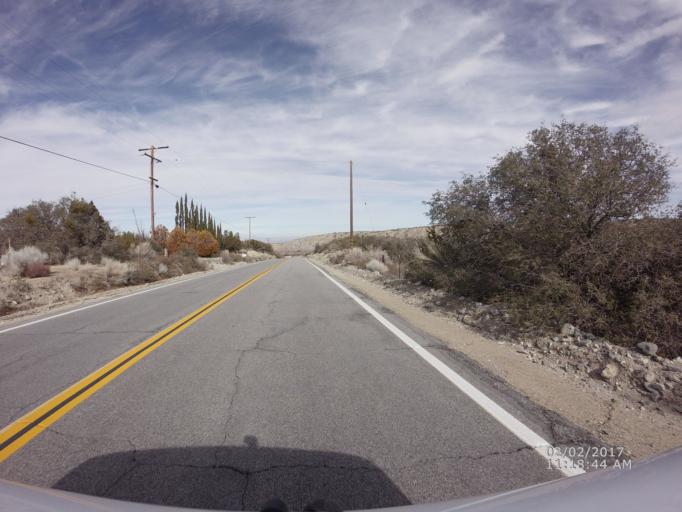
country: US
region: California
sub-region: Los Angeles County
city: Littlerock
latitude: 34.4372
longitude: -117.8965
